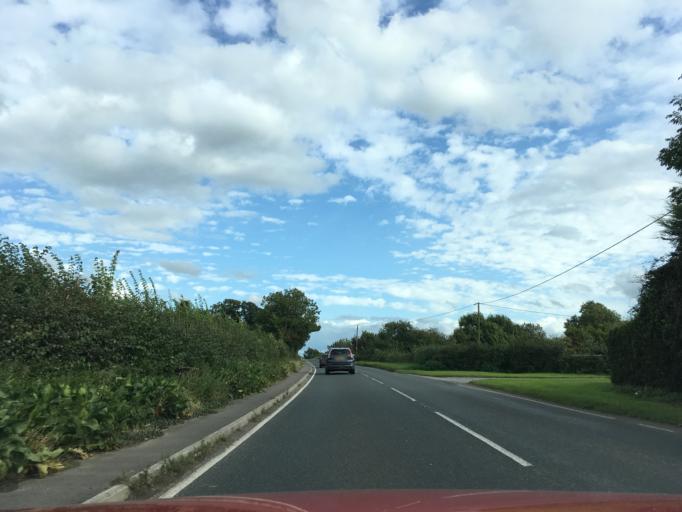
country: GB
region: England
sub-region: South Gloucestershire
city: Charfield
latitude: 51.6314
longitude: -2.4279
